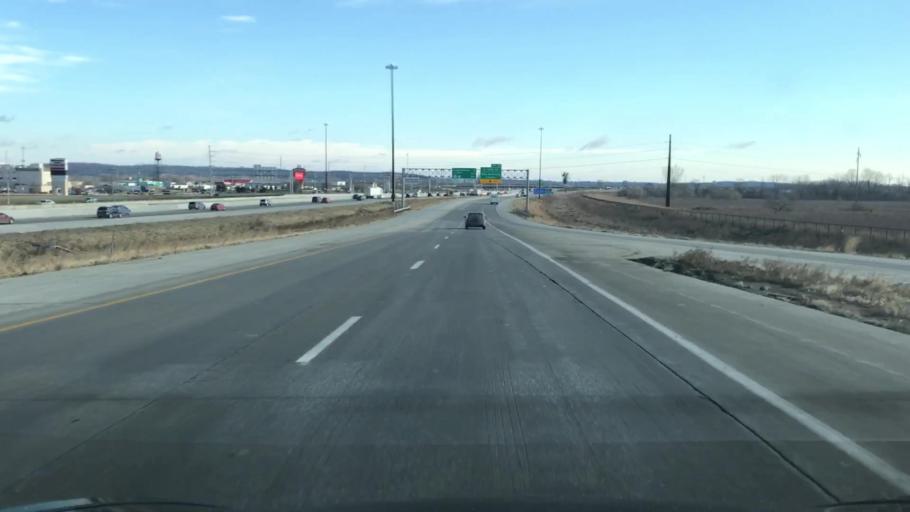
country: US
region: Iowa
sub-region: Pottawattamie County
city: Council Bluffs
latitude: 41.2319
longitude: -95.8932
